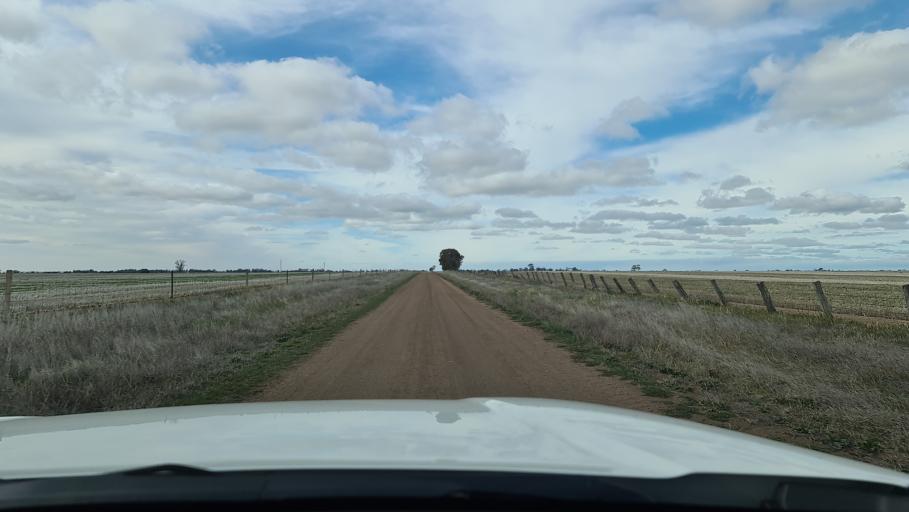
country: AU
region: Victoria
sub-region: Horsham
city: Horsham
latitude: -36.6311
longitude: 142.4258
